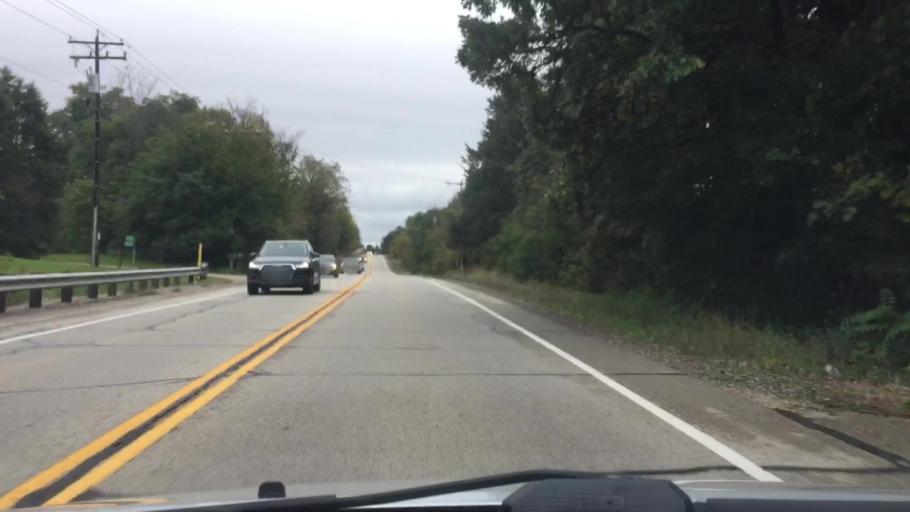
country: US
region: Wisconsin
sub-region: Jefferson County
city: Palmyra
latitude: 42.7851
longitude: -88.5601
